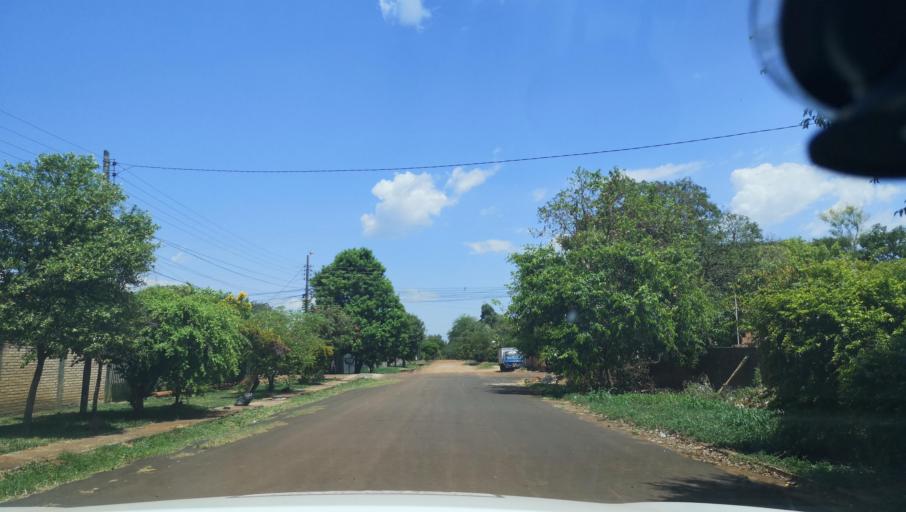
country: PY
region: Itapua
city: Carmen del Parana
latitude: -27.1652
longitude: -56.2344
